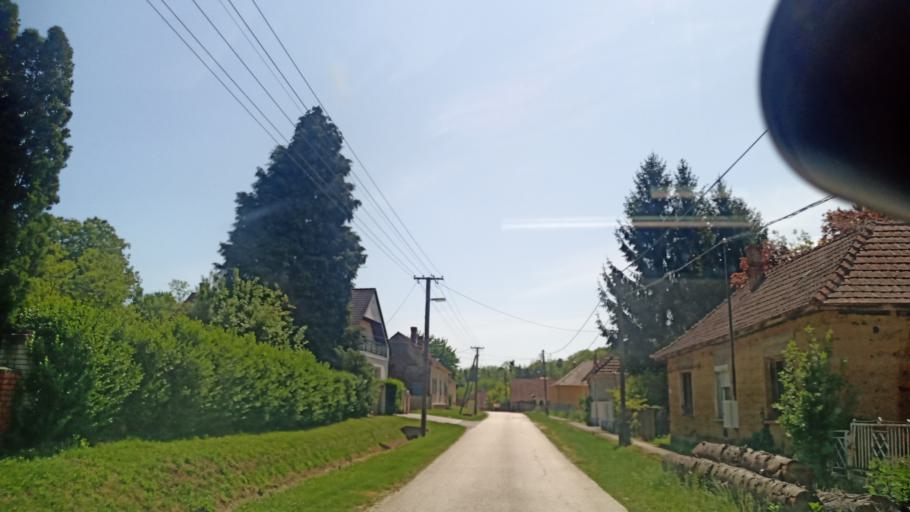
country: HU
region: Zala
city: Zalakomar
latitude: 46.6200
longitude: 17.1091
